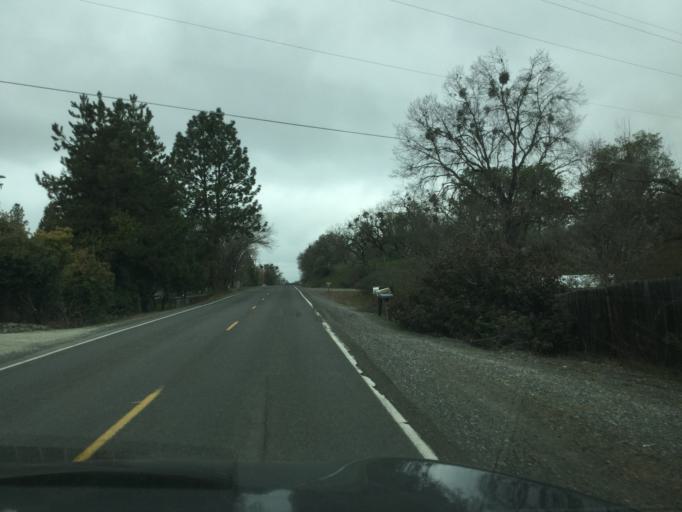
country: US
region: Oregon
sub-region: Jackson County
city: Central Point
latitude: 42.3870
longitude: -122.9788
